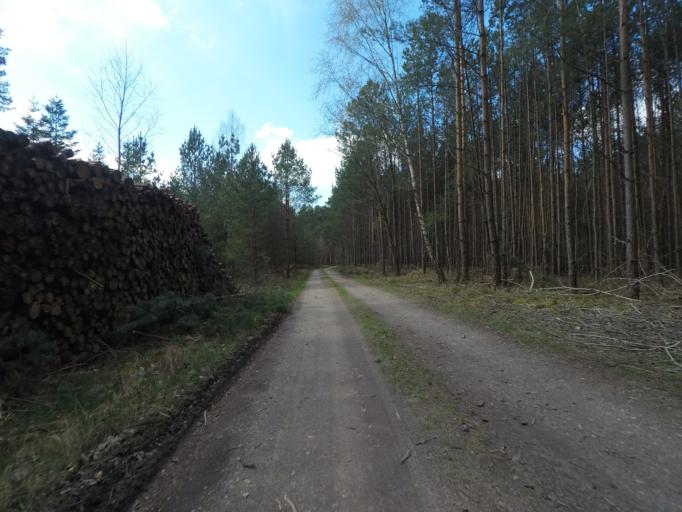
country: DE
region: Brandenburg
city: Melchow
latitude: 52.8158
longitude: 13.7035
